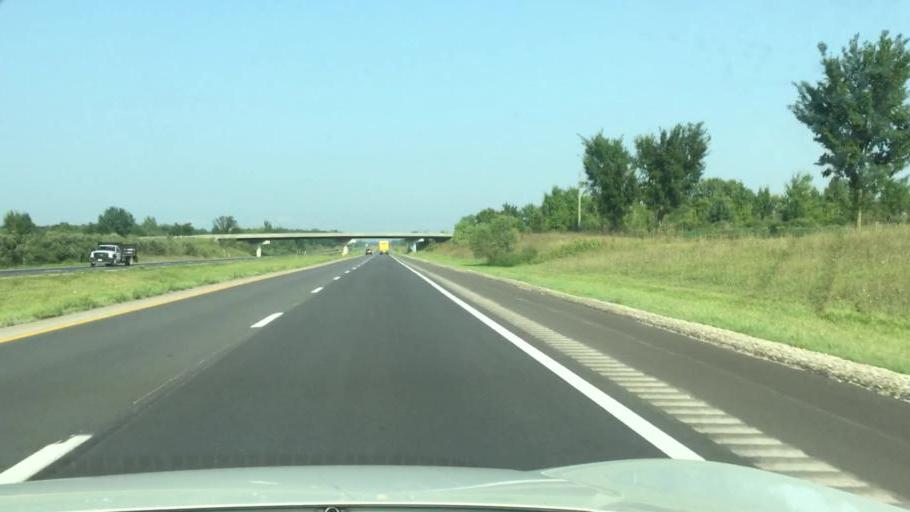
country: US
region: Ohio
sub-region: Union County
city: Marysville
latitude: 40.2561
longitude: -83.4528
